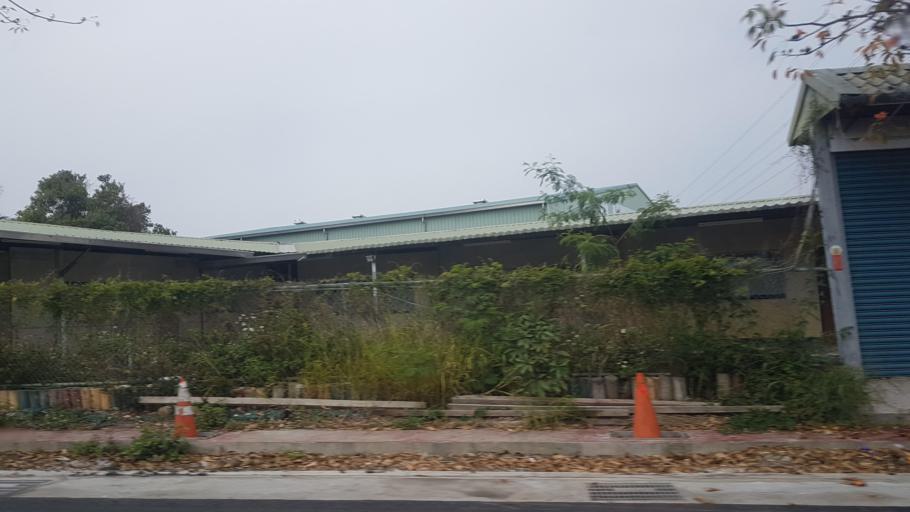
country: TW
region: Taiwan
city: Xinying
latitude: 23.3117
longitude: 120.2977
